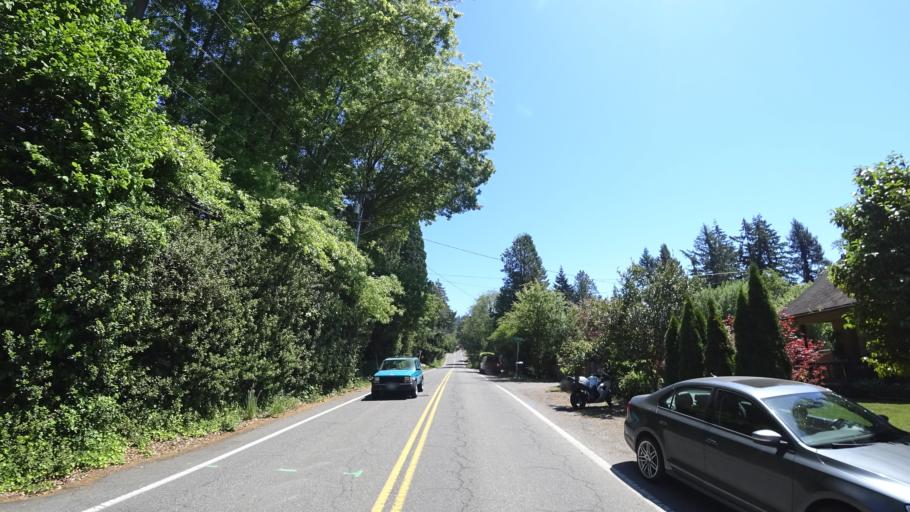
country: US
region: Oregon
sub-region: Washington County
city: Raleigh Hills
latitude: 45.4907
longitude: -122.7188
